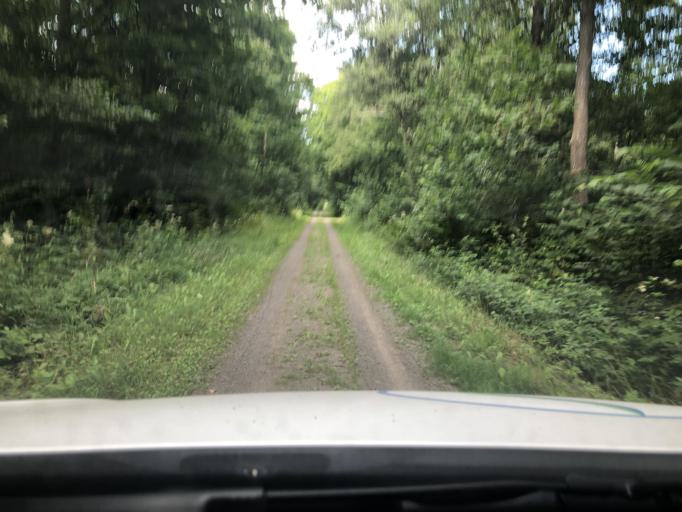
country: SE
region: Skane
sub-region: Kristianstads Kommun
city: Degeberga
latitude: 55.7788
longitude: 14.1703
